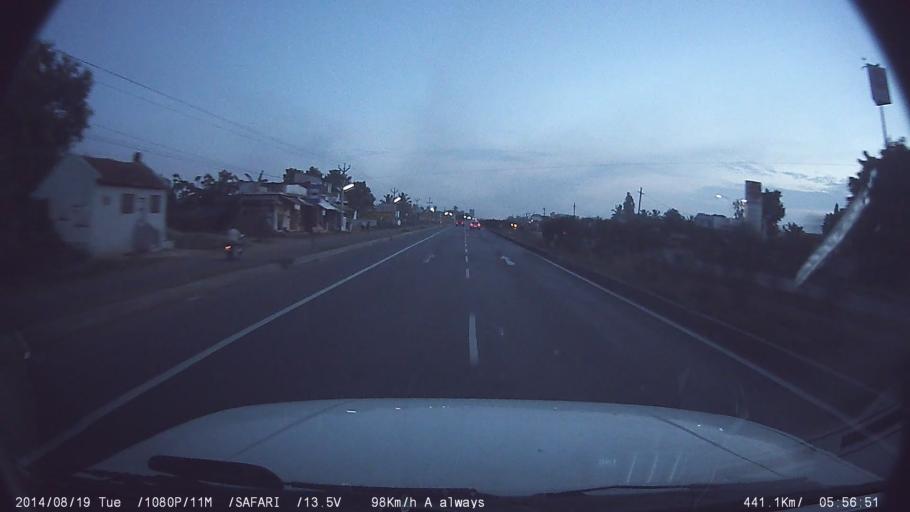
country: IN
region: Tamil Nadu
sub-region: Salem
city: Omalur
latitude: 11.7642
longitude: 78.0520
